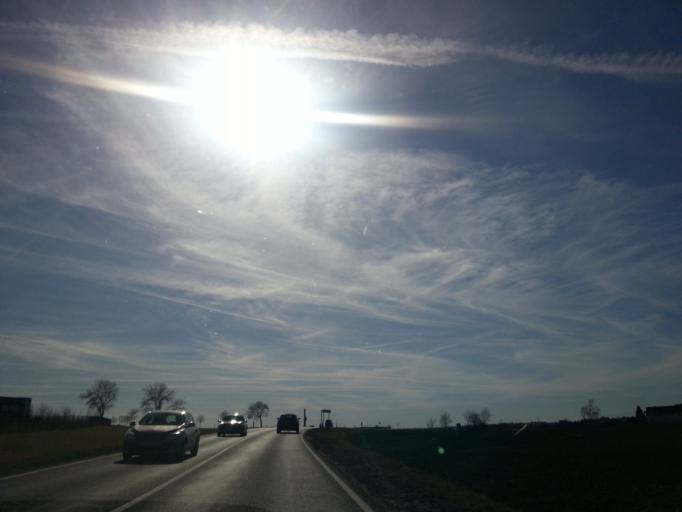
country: DE
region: Saxony
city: Halsbrucke
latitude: 50.9241
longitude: 13.3915
